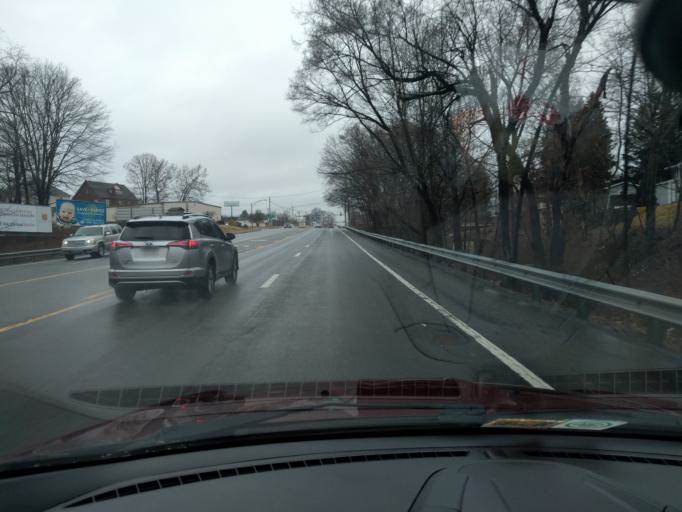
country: US
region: West Virginia
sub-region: Raleigh County
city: Beckley
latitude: 37.7696
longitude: -81.1957
